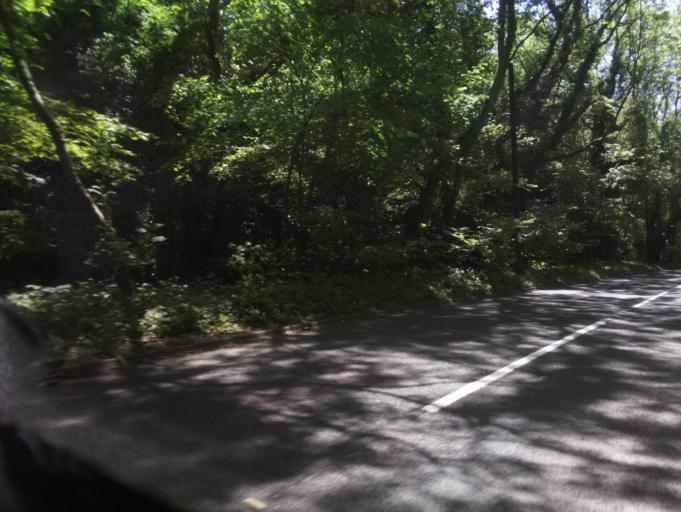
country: GB
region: Wales
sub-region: Monmouthshire
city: Caldicot
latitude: 51.6178
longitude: -2.7330
